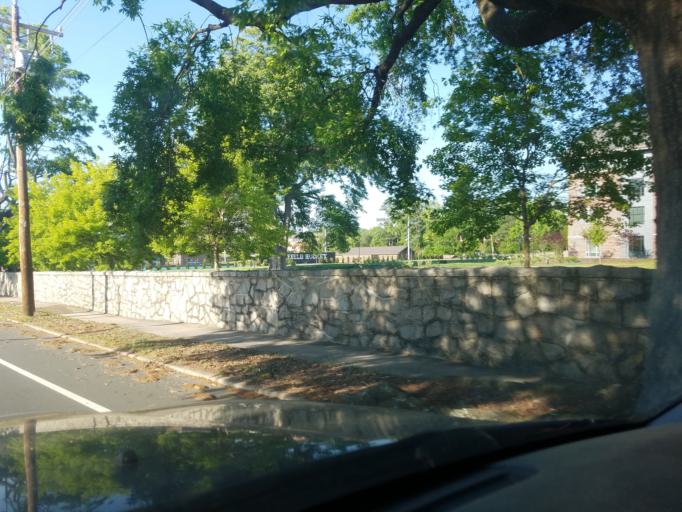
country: US
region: North Carolina
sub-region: Durham County
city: Durham
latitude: 36.0067
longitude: -78.9198
